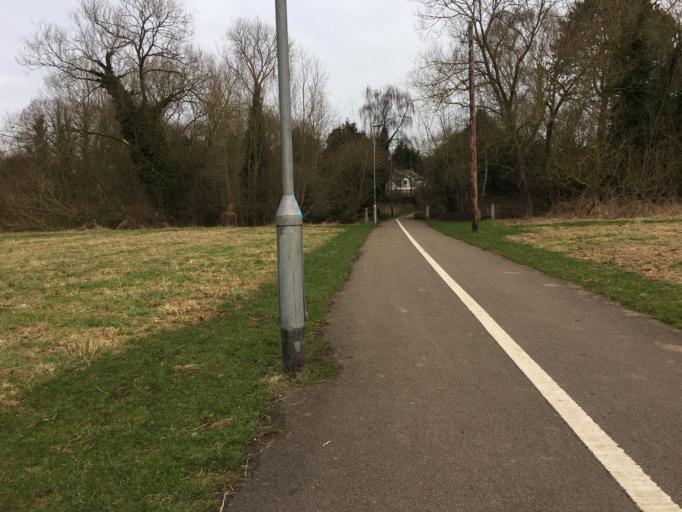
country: GB
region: England
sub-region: Warwickshire
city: Rugby
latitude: 52.3841
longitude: -1.2456
